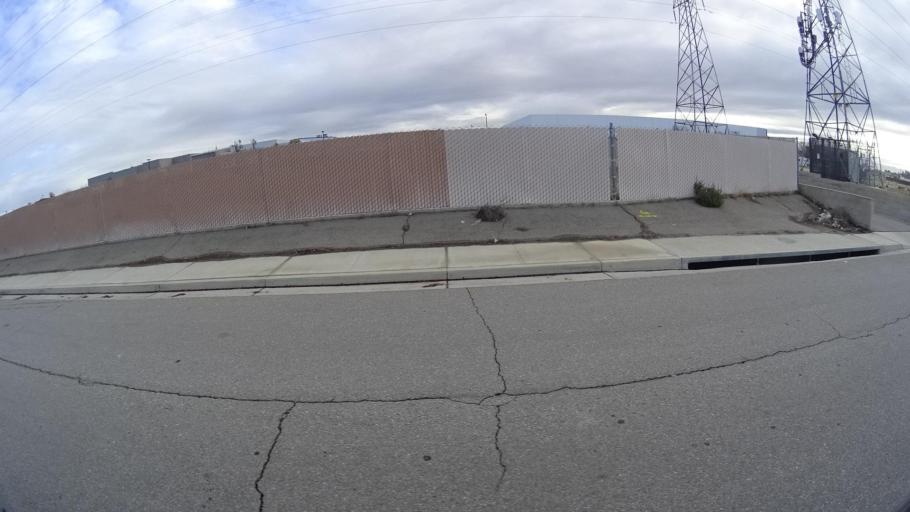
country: US
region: California
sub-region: Kern County
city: Greenacres
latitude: 35.4461
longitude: -119.0831
